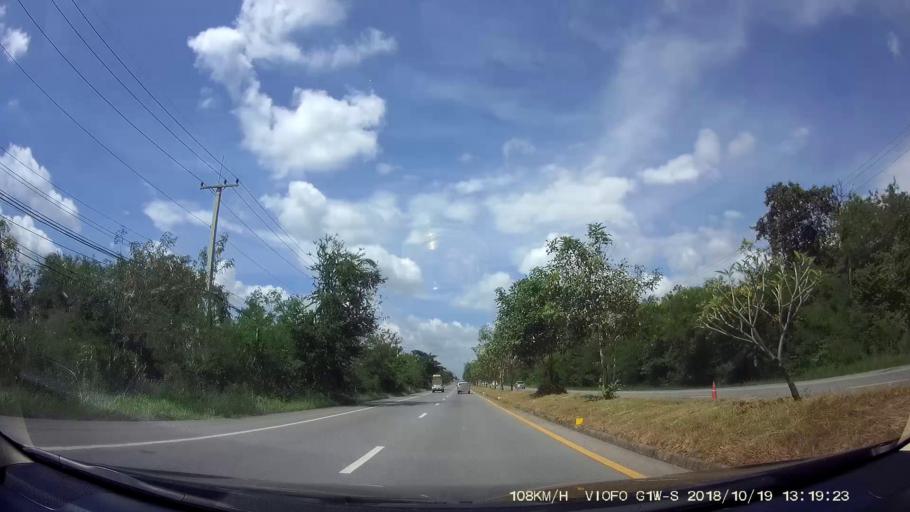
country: TH
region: Chaiyaphum
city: Chatturat
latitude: 15.4290
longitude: 101.8312
